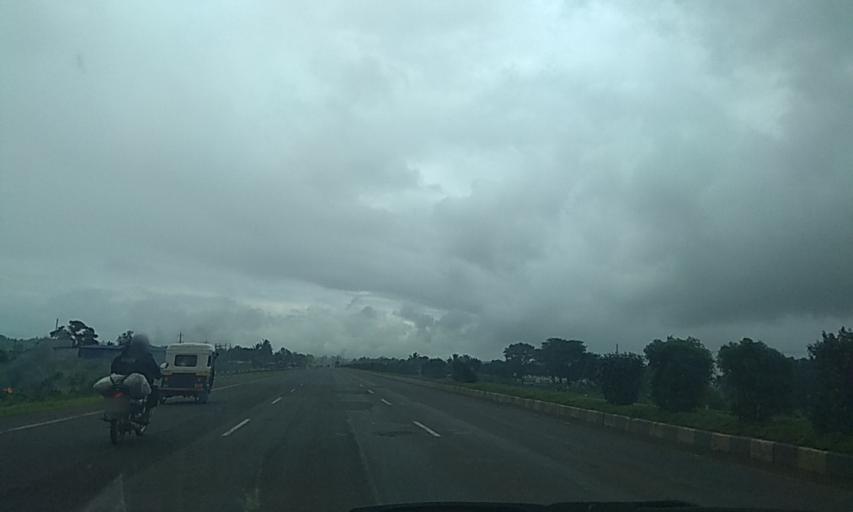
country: IN
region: Karnataka
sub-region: Belgaum
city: Belgaum
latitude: 15.8457
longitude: 74.5389
